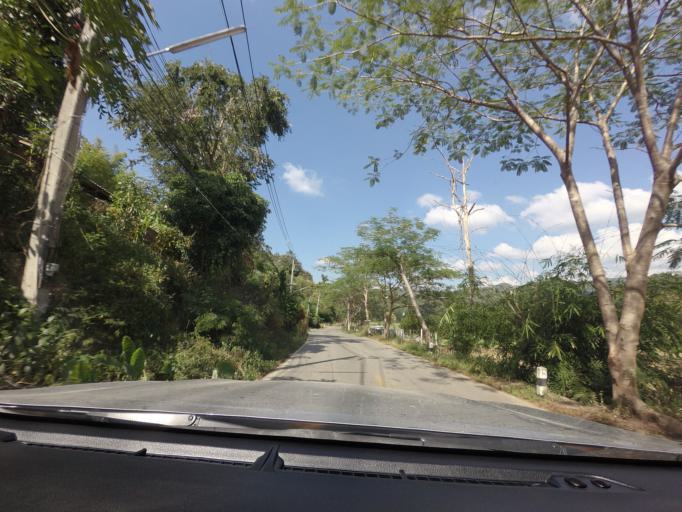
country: TH
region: Chiang Mai
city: Mae On
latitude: 18.8874
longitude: 99.2638
